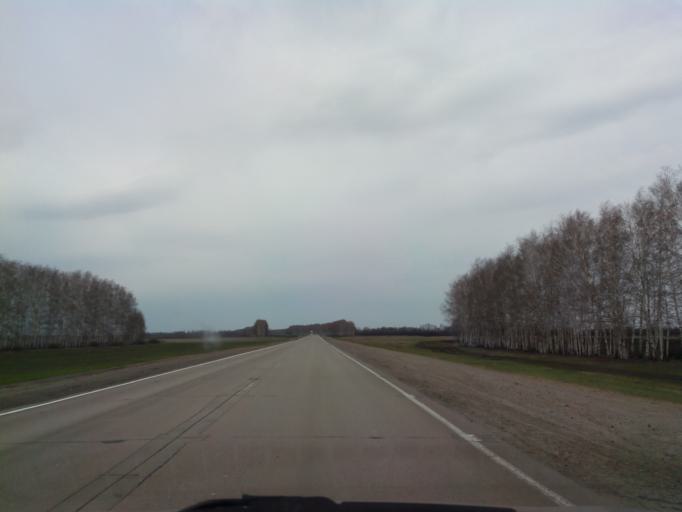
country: RU
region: Tambov
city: Znamenka
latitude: 52.2411
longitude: 41.5303
